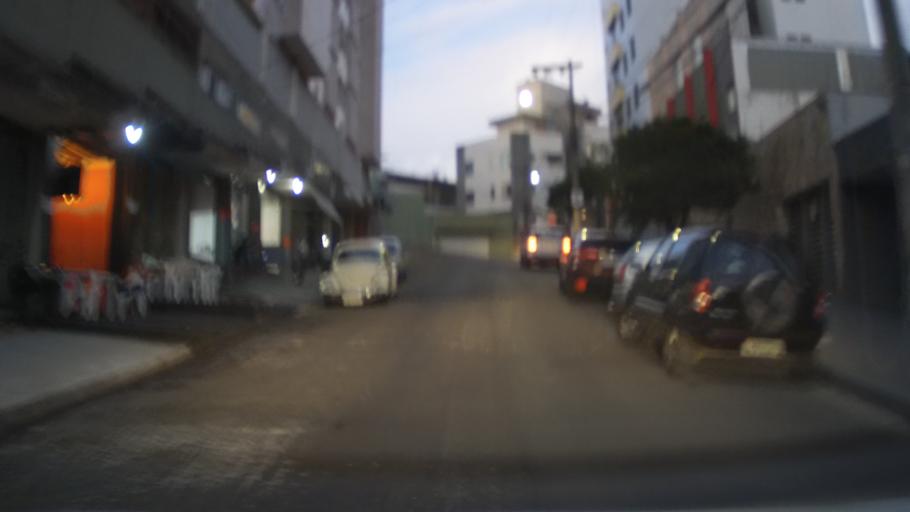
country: BR
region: Minas Gerais
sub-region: Belo Horizonte
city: Belo Horizonte
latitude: -19.9053
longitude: -43.9380
